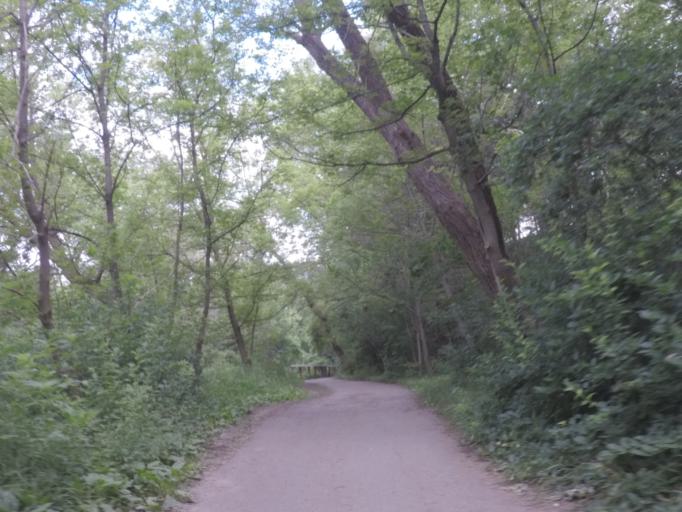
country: CA
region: Ontario
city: Etobicoke
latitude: 43.6543
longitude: -79.5473
